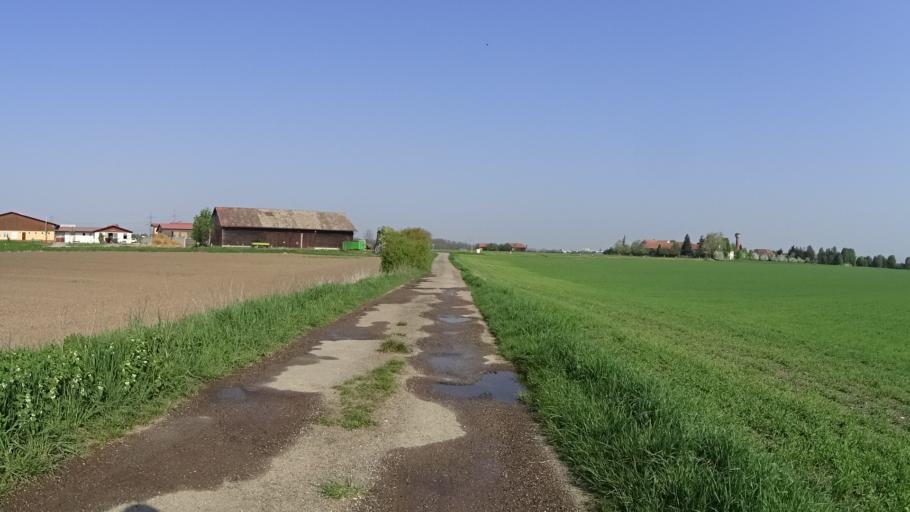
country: DE
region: Baden-Wuerttemberg
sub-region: Karlsruhe Region
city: Heddesheim
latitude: 49.5077
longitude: 8.5764
